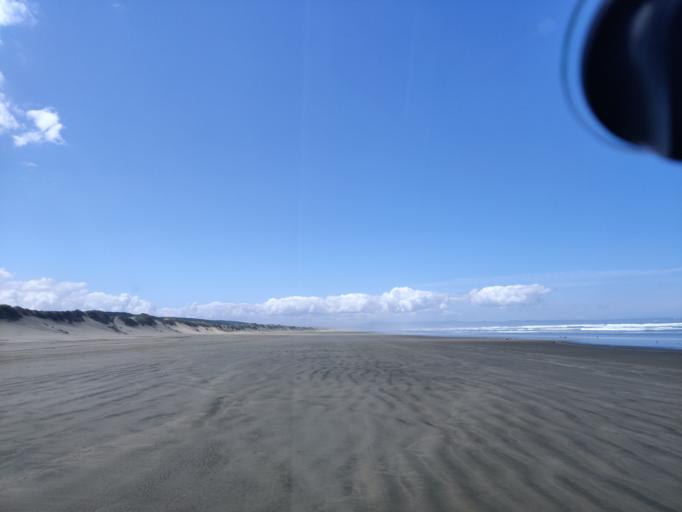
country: NZ
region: Northland
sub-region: Far North District
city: Kaitaia
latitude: -34.9481
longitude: 173.1202
